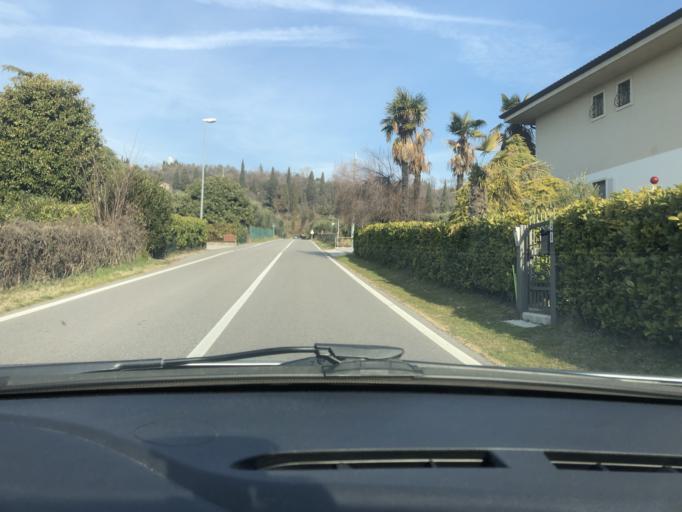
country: IT
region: Veneto
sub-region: Provincia di Verona
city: Garda
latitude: 45.5605
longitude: 10.7249
